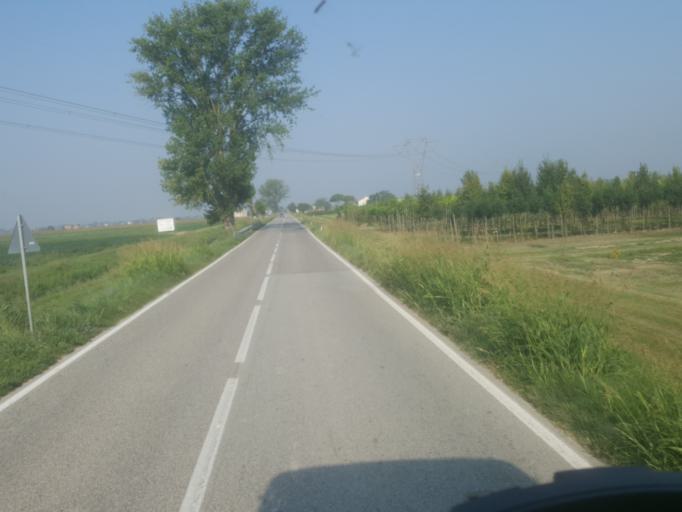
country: IT
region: Emilia-Romagna
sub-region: Provincia di Ravenna
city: Voltana
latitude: 44.5565
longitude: 11.9280
